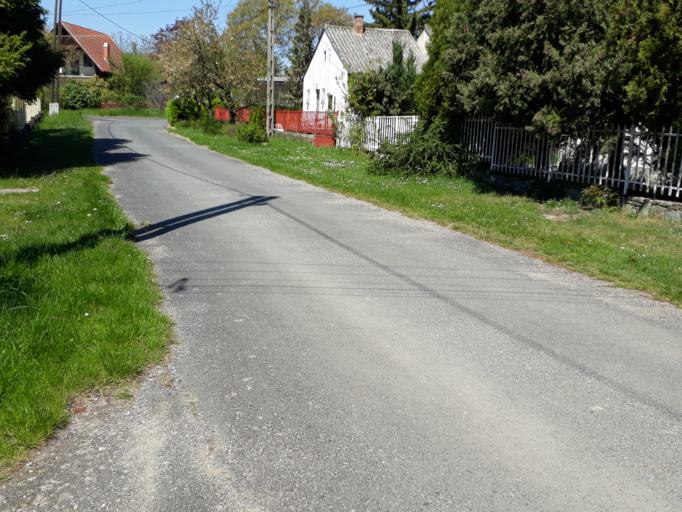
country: HU
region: Veszprem
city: Zanka
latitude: 46.8689
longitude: 17.6840
